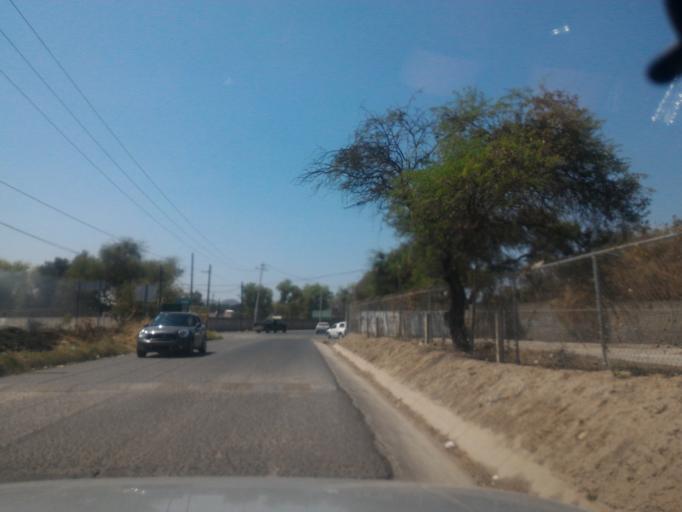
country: MX
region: Jalisco
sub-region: San Pedro Tlaquepaque
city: Santa Anita
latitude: 20.5518
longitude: -103.4339
